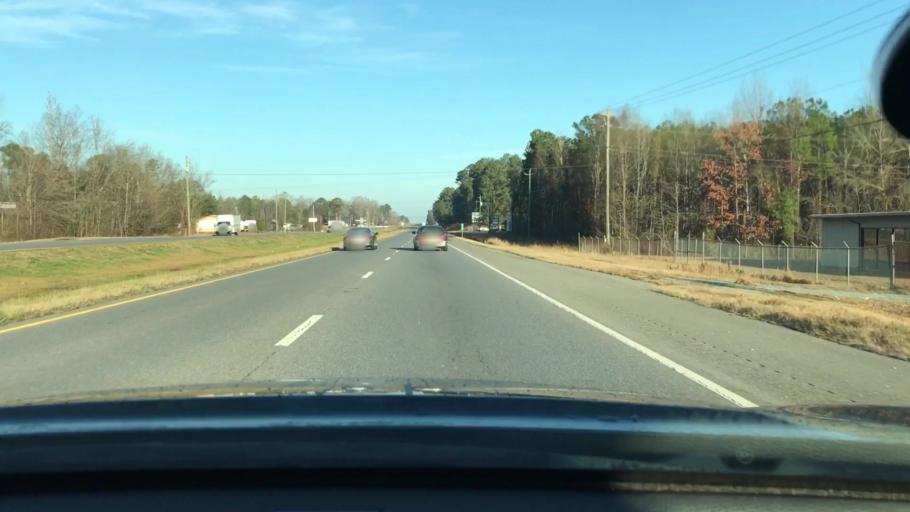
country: US
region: Alabama
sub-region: Talladega County
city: Childersburg
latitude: 33.2362
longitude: -86.3302
